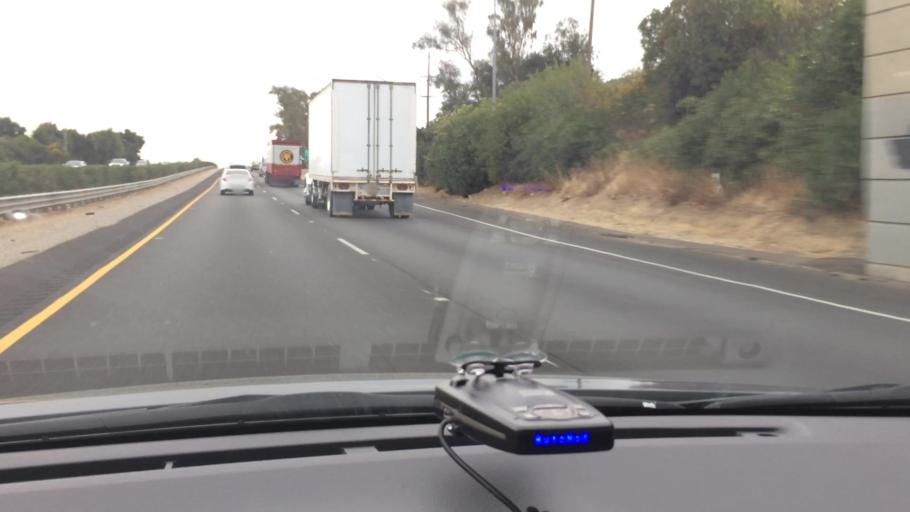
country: US
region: California
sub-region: San Joaquin County
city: Collierville
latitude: 38.1747
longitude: -121.2623
